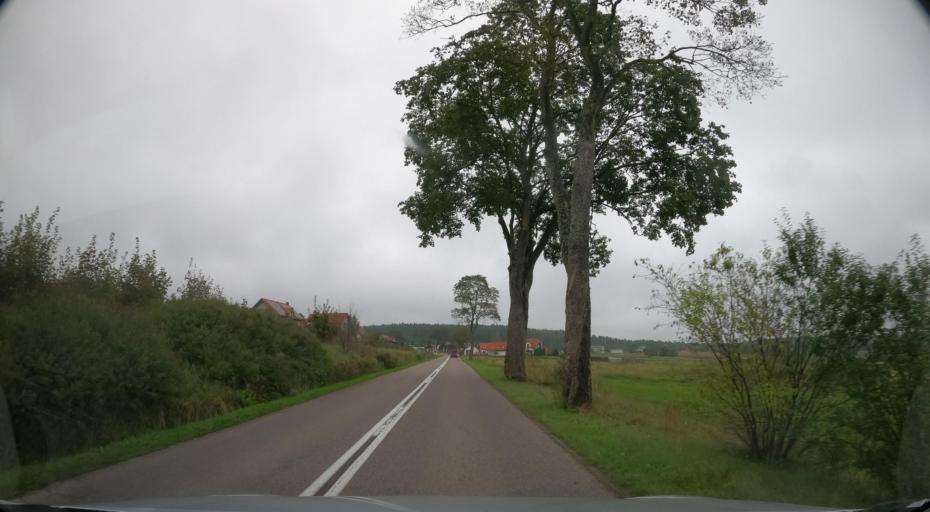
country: PL
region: Pomeranian Voivodeship
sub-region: Powiat wejherowski
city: Luzino
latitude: 54.4673
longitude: 18.0687
